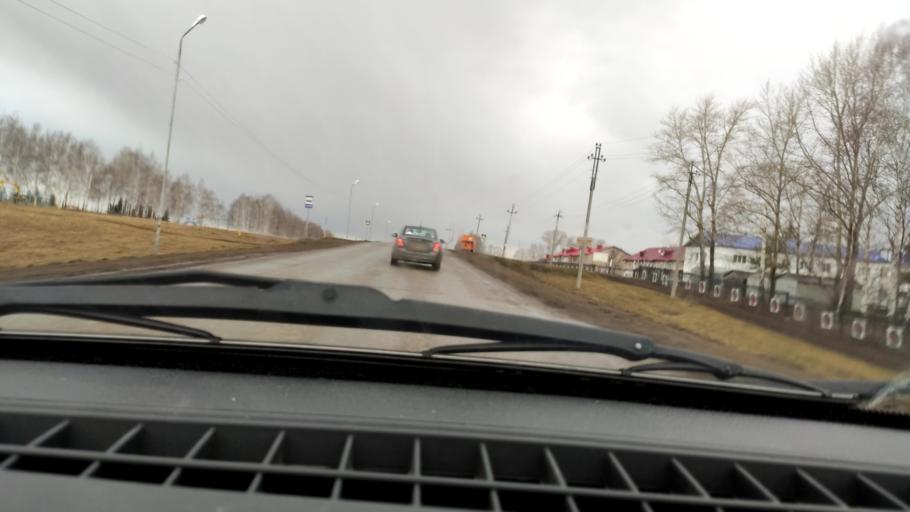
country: RU
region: Bashkortostan
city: Chekmagush
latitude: 55.1158
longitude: 54.8461
